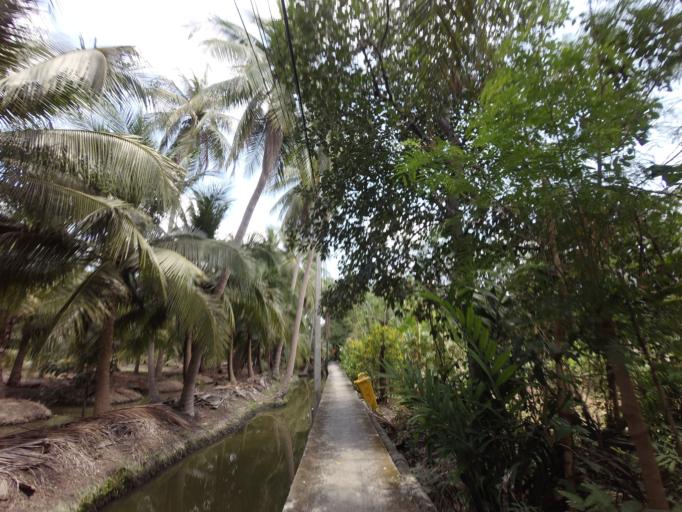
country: TH
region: Bangkok
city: Chom Thong
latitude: 13.6576
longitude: 100.4882
